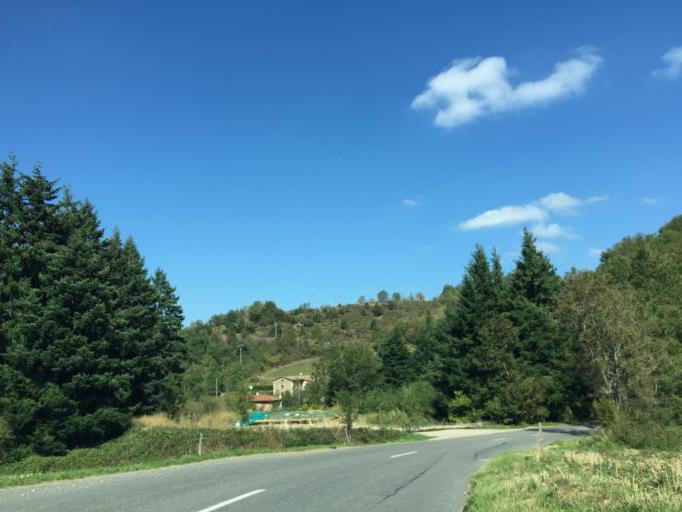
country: FR
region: Rhone-Alpes
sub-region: Departement de la Loire
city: Saint-Paul-en-Jarez
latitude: 45.4332
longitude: 4.5756
